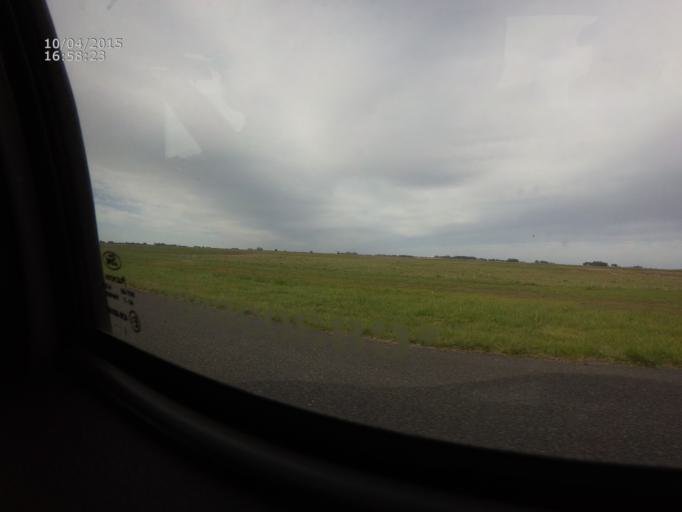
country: AR
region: Buenos Aires
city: Coronel Vidal
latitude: -37.4930
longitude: -57.7165
